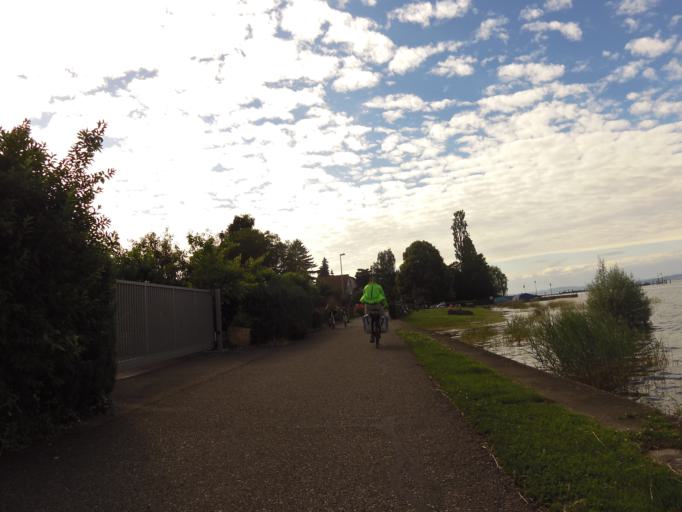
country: CH
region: Thurgau
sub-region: Arbon District
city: Uttwil
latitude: 47.5843
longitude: 9.3476
